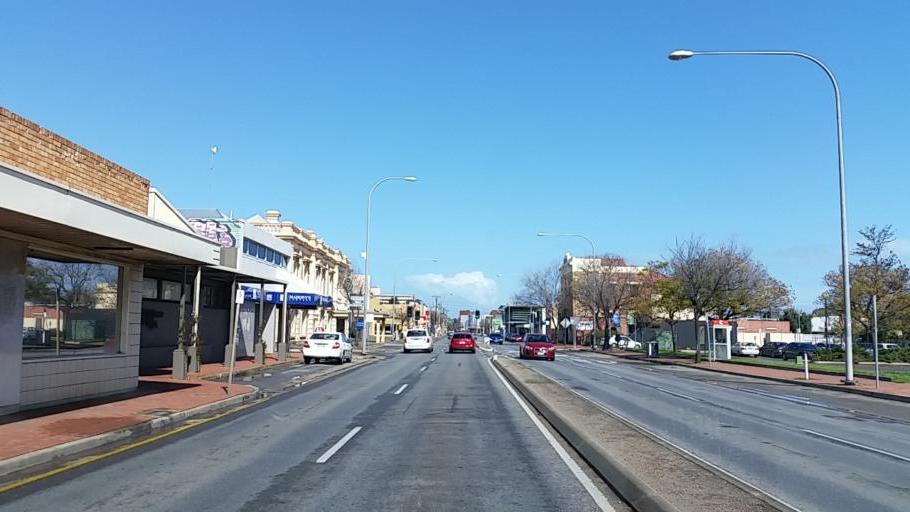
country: AU
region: South Australia
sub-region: Charles Sturt
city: Woodville North
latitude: -34.8777
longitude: 138.5381
